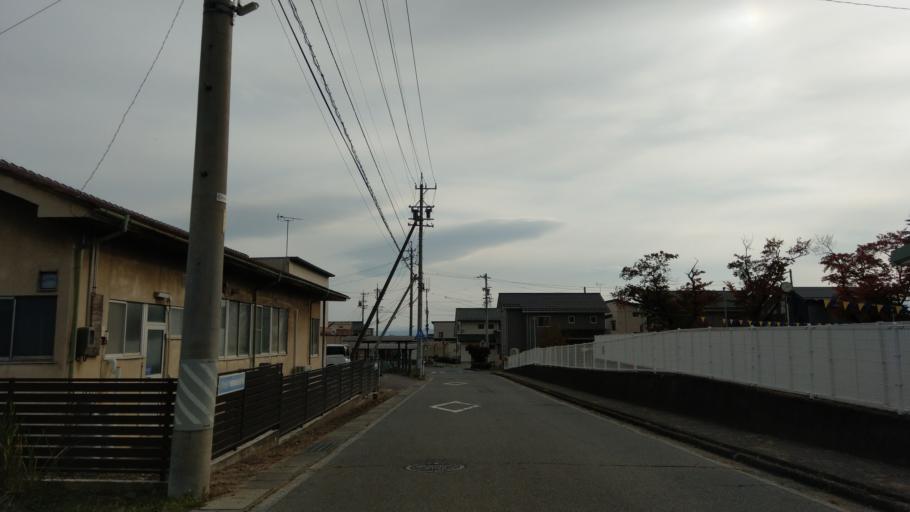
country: JP
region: Nagano
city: Komoro
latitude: 36.3173
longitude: 138.4409
